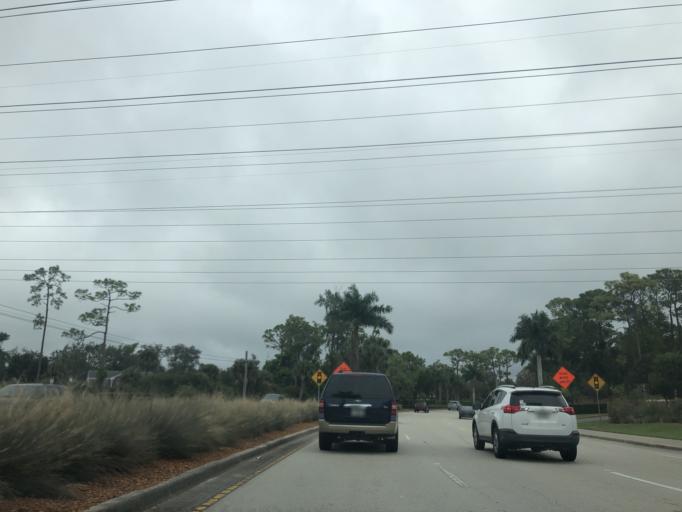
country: US
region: Florida
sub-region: Palm Beach County
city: Wellington
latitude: 26.6766
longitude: -80.2484
